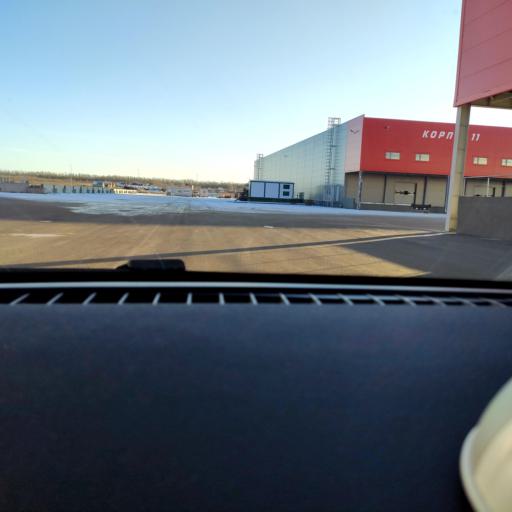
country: RU
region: Samara
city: Samara
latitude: 53.0916
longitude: 50.1288
